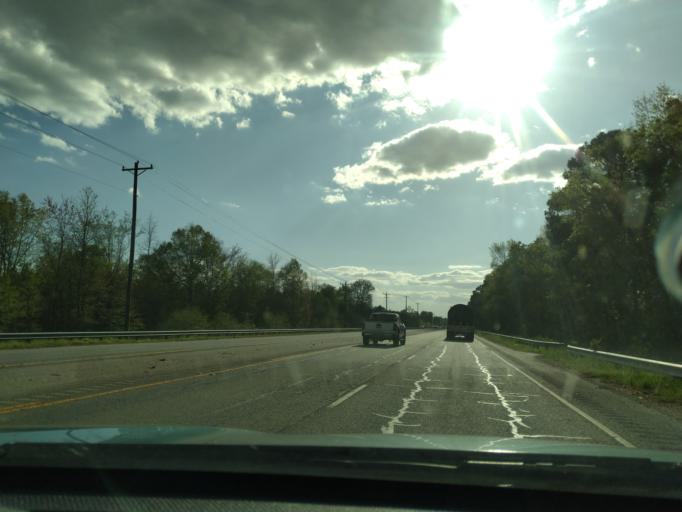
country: US
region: South Carolina
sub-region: Williamsburg County
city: Kingstree
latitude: 33.6608
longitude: -79.8429
